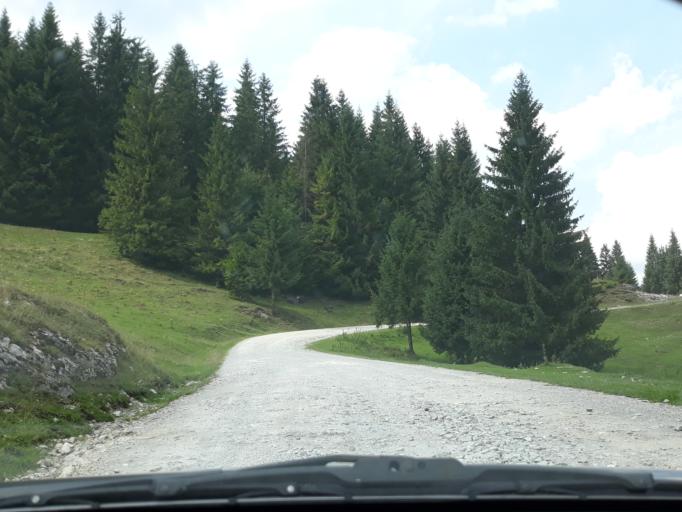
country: RO
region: Bihor
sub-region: Comuna Pietroasa
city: Pietroasa
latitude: 46.5912
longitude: 22.6842
